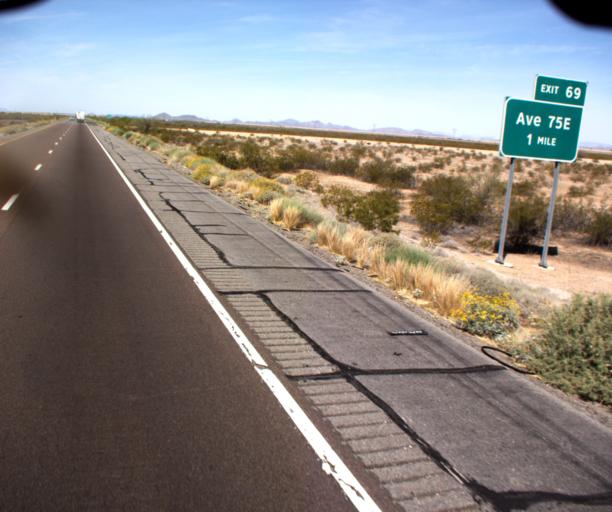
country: US
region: Arizona
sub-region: La Paz County
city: Salome
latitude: 33.5660
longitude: -113.3312
